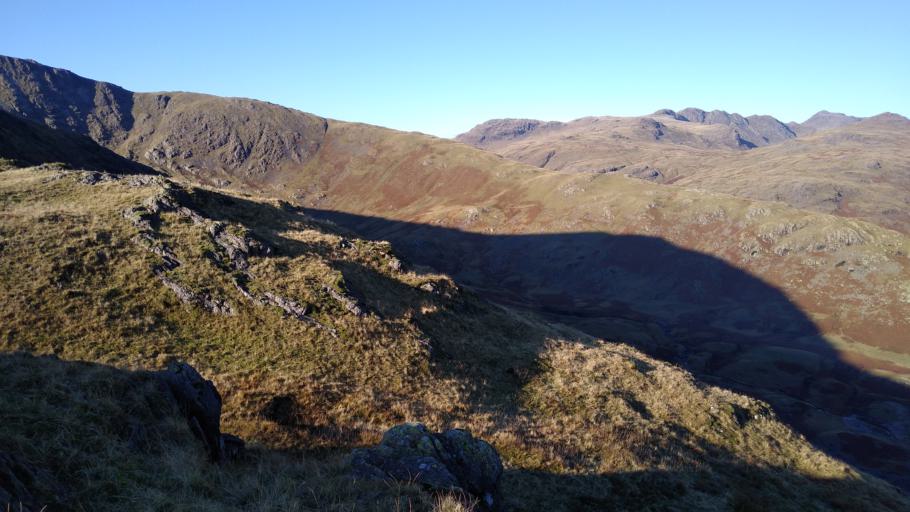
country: GB
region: England
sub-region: Cumbria
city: Ambleside
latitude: 54.4055
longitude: -3.0888
